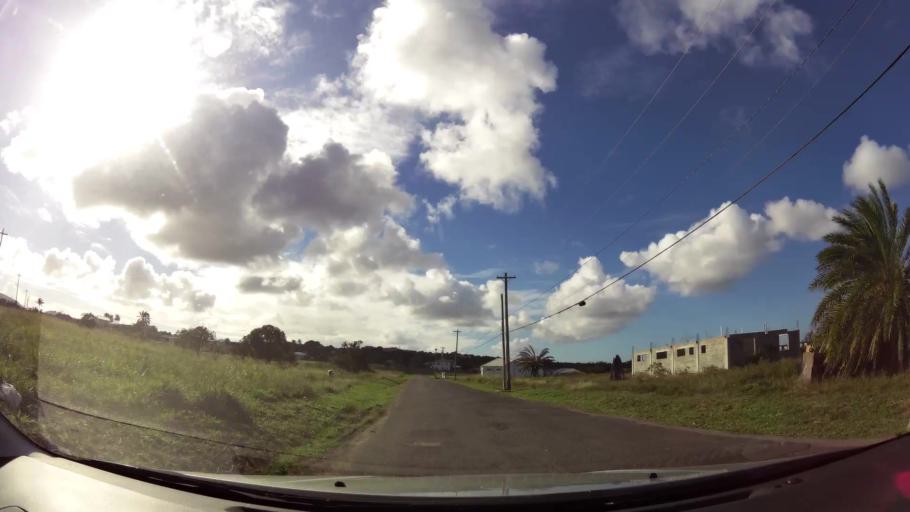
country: AG
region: Saint Peter
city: All Saints
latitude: 17.0786
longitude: -61.7810
